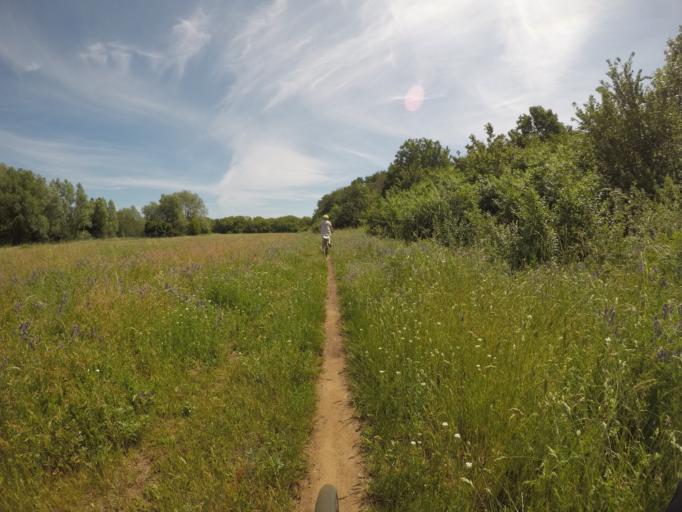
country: DE
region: Berlin
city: Kaulsdorf
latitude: 52.4976
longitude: 13.5917
